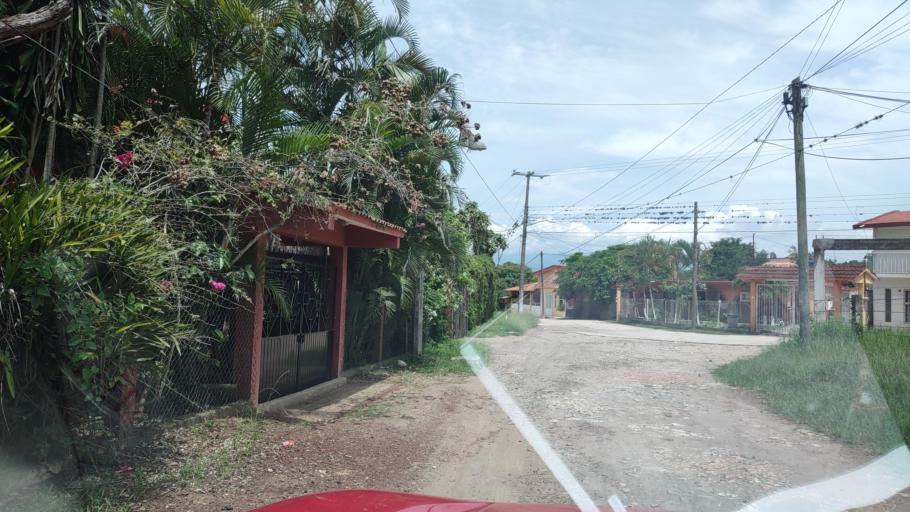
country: MX
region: Veracruz
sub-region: Emiliano Zapata
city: Jacarandas
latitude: 19.4664
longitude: -96.8329
